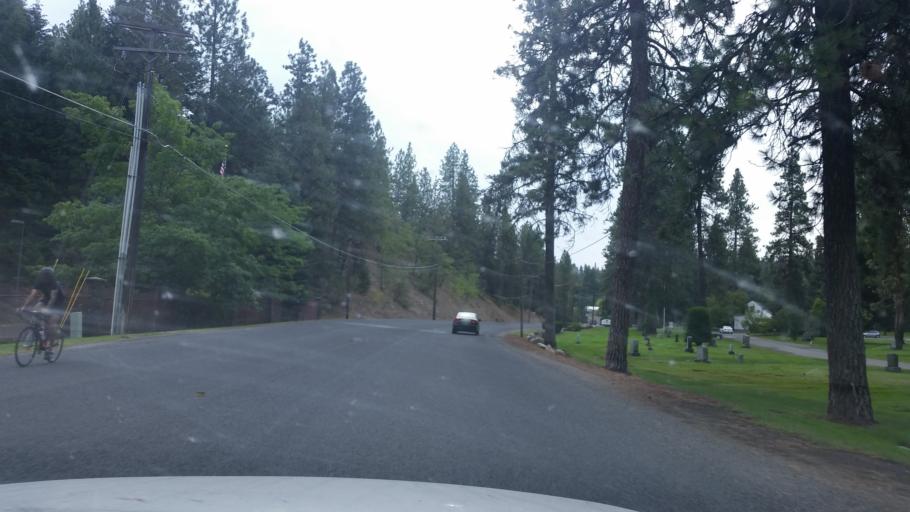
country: US
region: Washington
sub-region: Spokane County
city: Spokane
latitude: 47.6602
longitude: -117.4663
